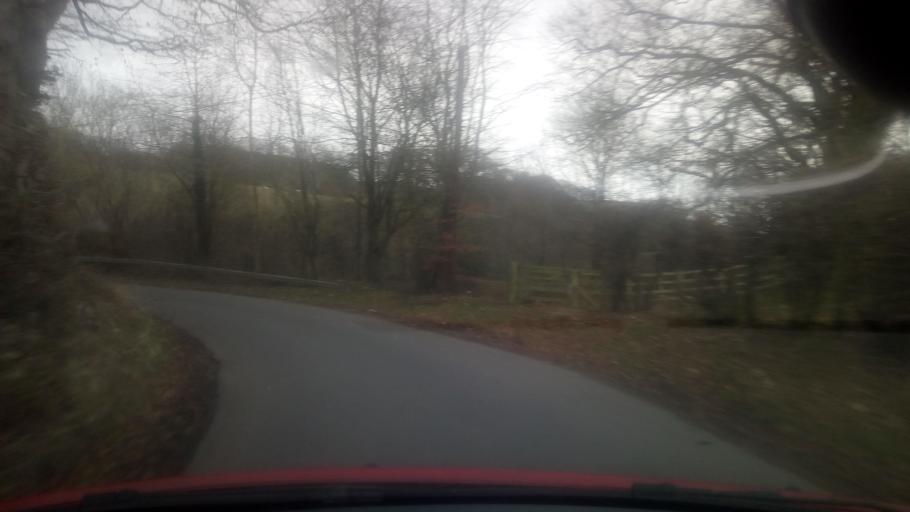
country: GB
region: Scotland
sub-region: The Scottish Borders
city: Jedburgh
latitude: 55.4743
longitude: -2.5407
